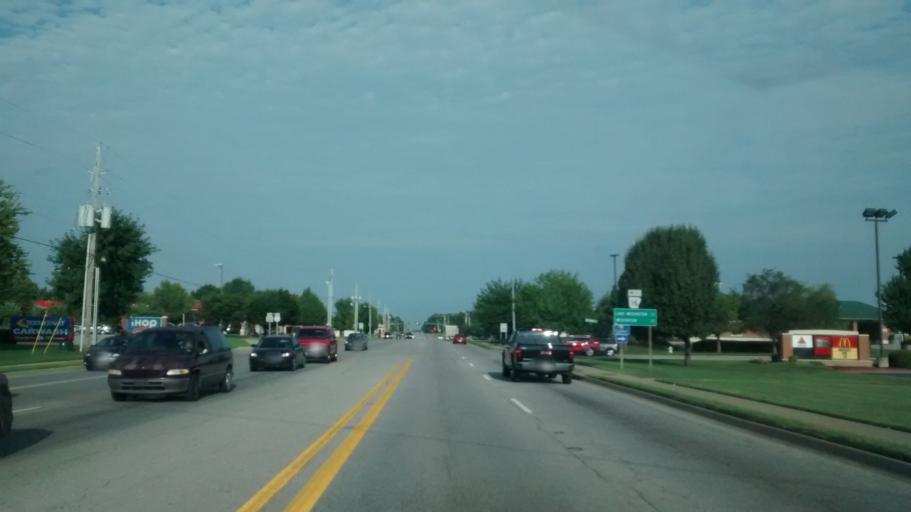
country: US
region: Arkansas
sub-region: Washington County
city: Fayetteville
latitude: 36.0784
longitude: -94.2030
